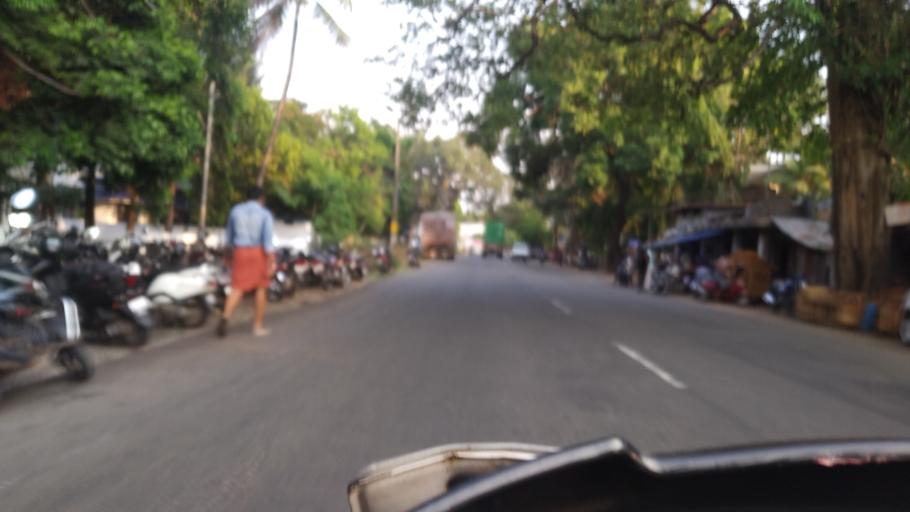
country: IN
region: Kerala
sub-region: Thrissur District
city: Irinjalakuda
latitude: 10.3327
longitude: 76.1404
